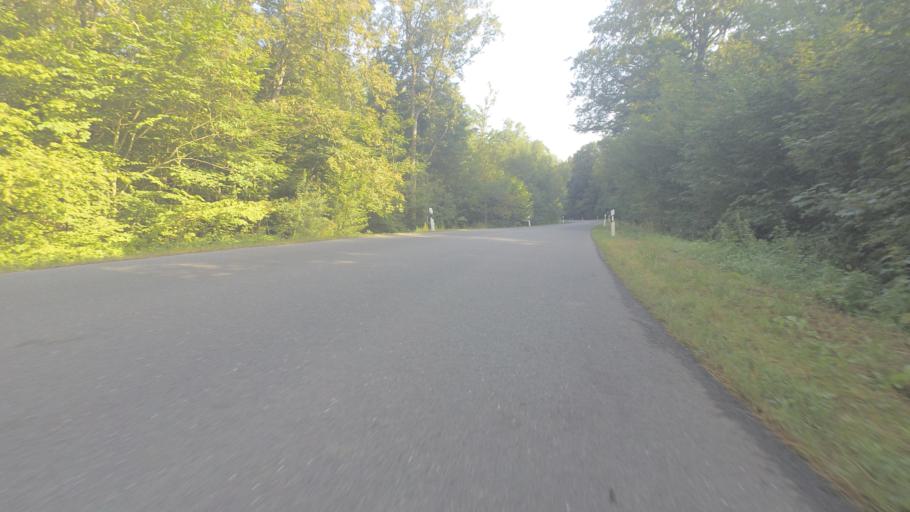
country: DE
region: Mecklenburg-Vorpommern
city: Grimmen
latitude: 54.1432
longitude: 13.0664
